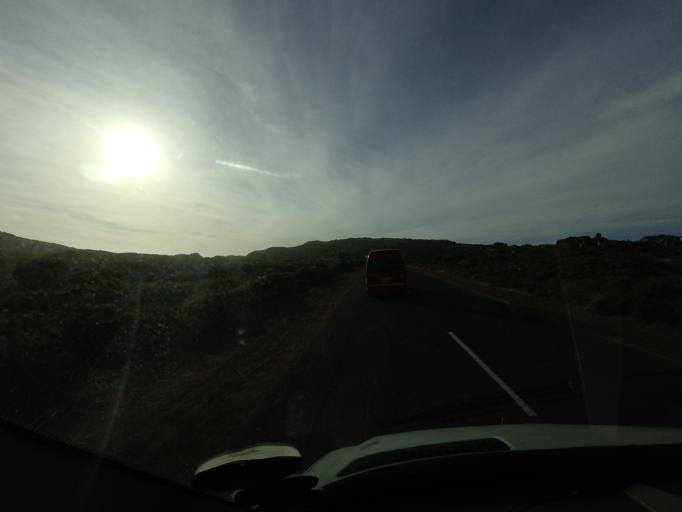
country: ZA
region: Western Cape
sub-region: City of Cape Town
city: Constantia
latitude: -34.1661
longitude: 18.3445
